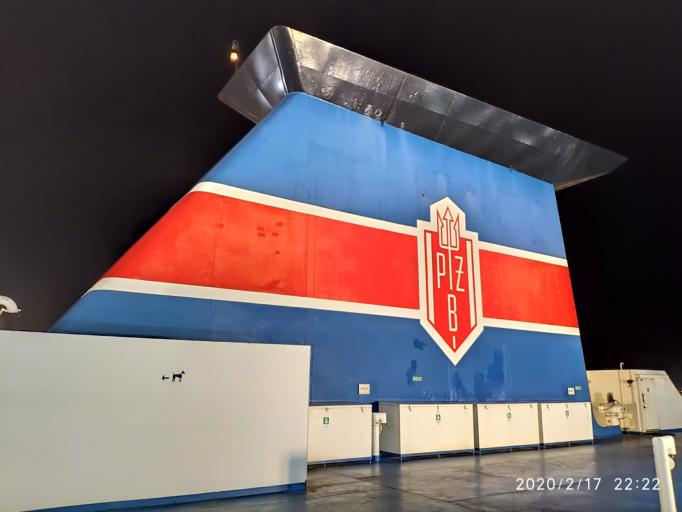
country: PL
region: West Pomeranian Voivodeship
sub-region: Swinoujscie
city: Swinoujscie
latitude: 53.8969
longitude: 14.2560
